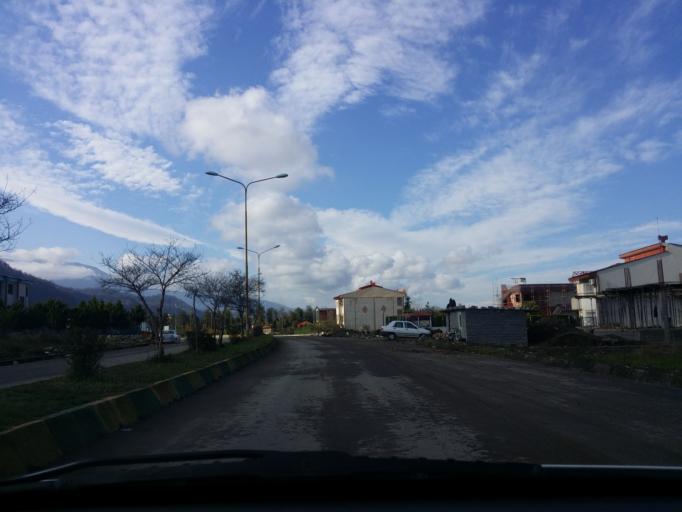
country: IR
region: Mazandaran
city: Chalus
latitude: 36.6759
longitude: 51.3019
